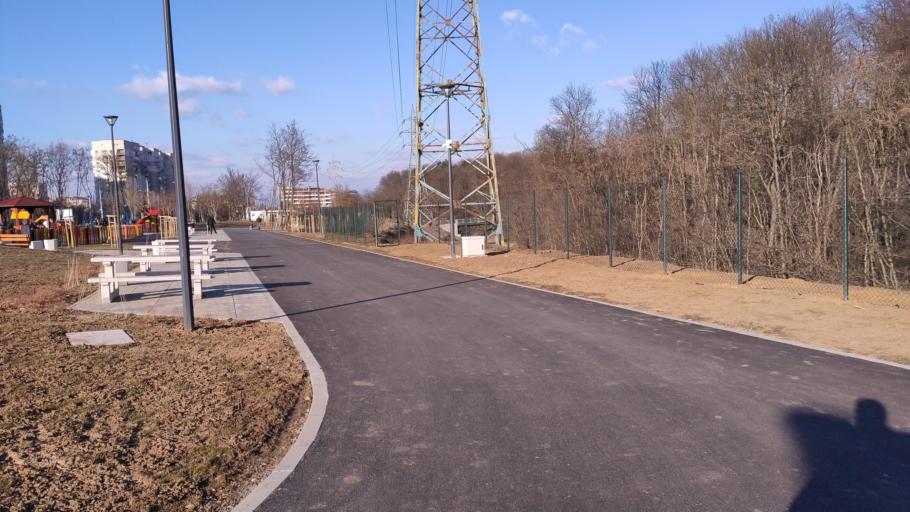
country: BG
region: Sofia-Capital
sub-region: Stolichna Obshtina
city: Sofia
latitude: 42.7116
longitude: 23.2743
